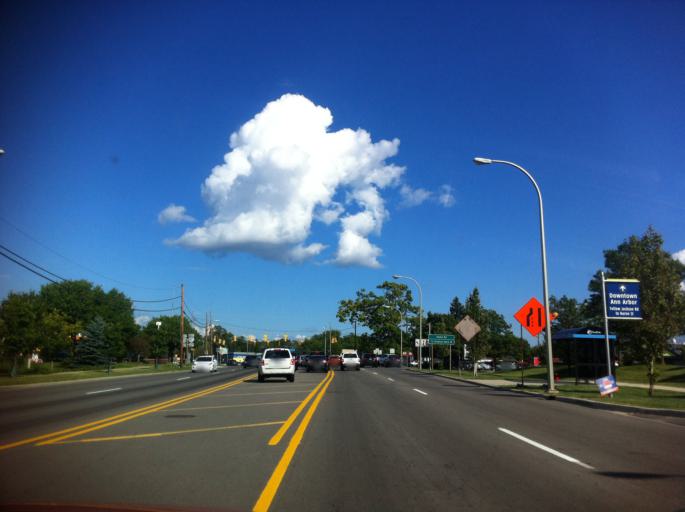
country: US
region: Michigan
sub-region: Washtenaw County
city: Ann Arbor
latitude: 42.2680
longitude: -83.7846
